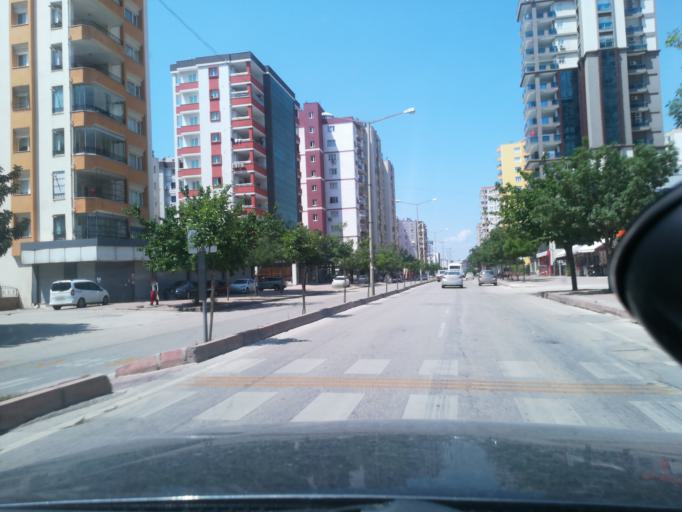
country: TR
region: Adana
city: Seyhan
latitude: 37.0346
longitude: 35.2635
